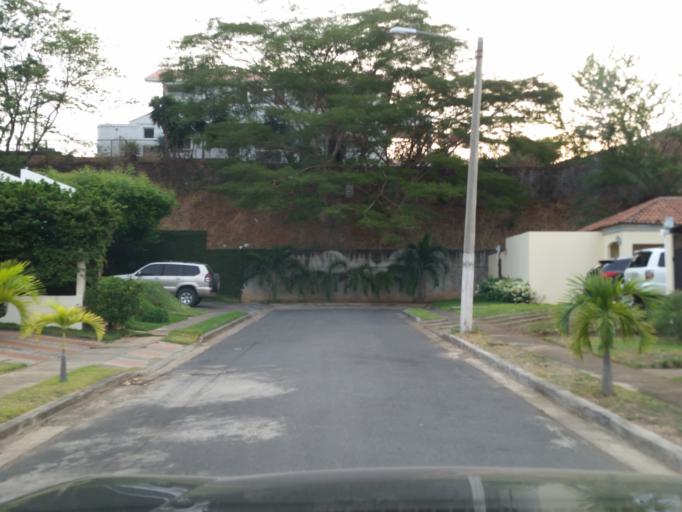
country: NI
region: Managua
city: Managua
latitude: 12.0976
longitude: -86.2555
